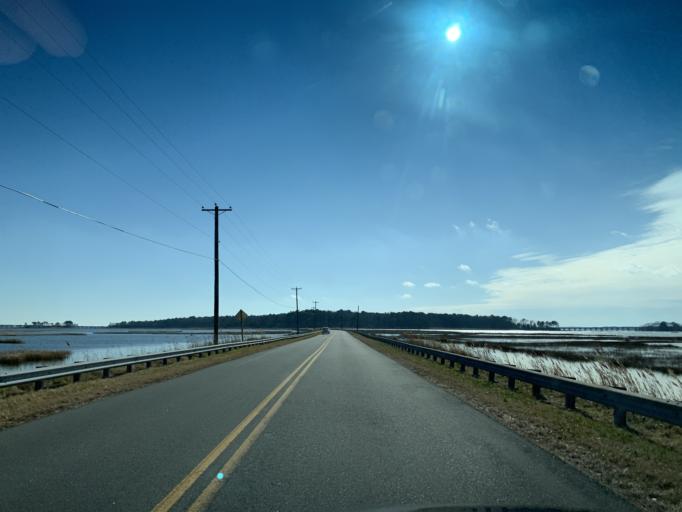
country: US
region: Maryland
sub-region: Worcester County
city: Ocean Pines
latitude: 38.4044
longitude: -75.1094
